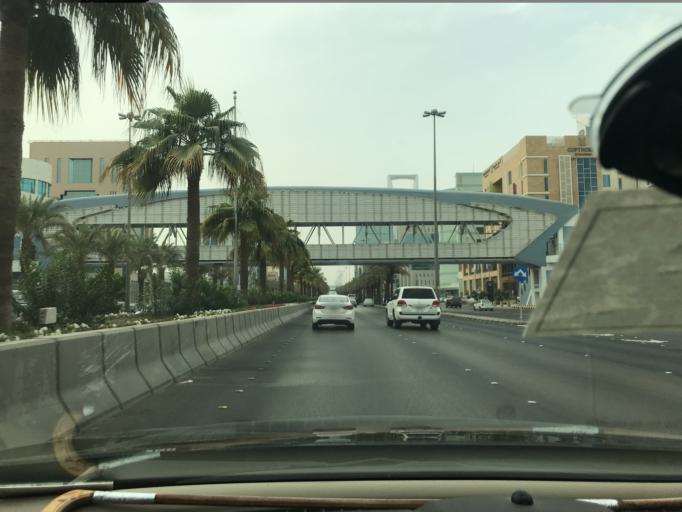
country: SA
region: Ar Riyad
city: Riyadh
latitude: 24.6992
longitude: 46.6785
